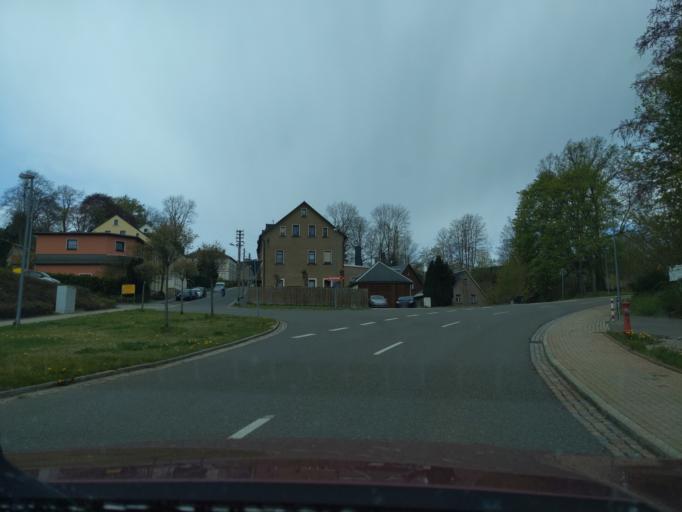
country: DE
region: Saxony
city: Schoenheide
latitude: 50.5037
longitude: 12.5239
